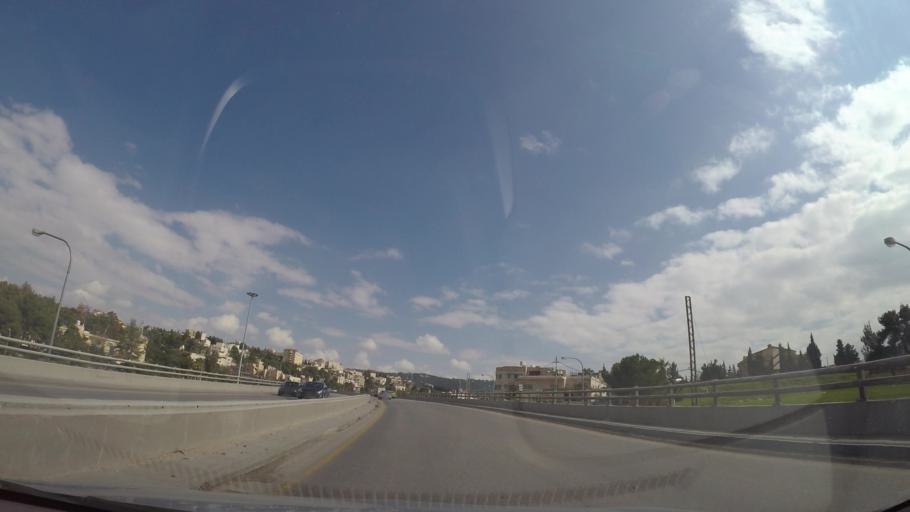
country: JO
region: Amman
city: Al Jubayhah
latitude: 32.0278
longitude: 35.7980
